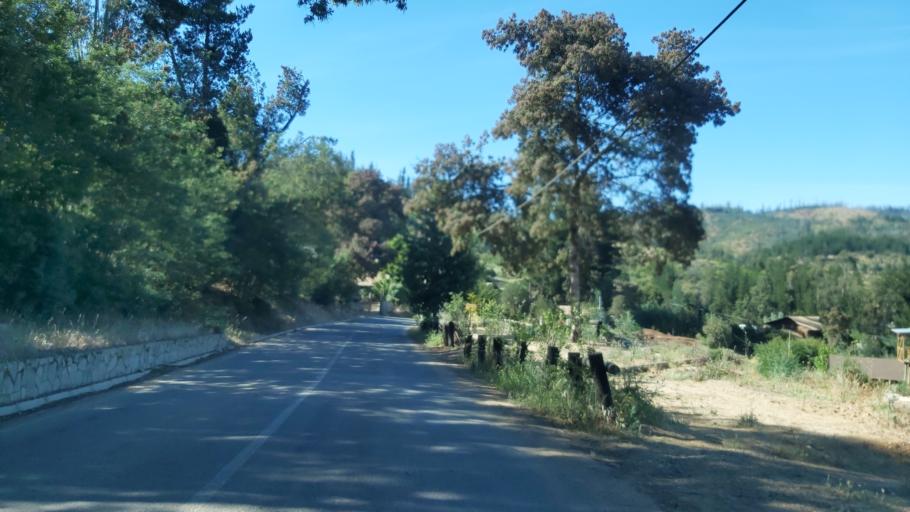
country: CL
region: Maule
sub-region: Provincia de Talca
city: Constitucion
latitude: -34.8433
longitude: -72.0521
